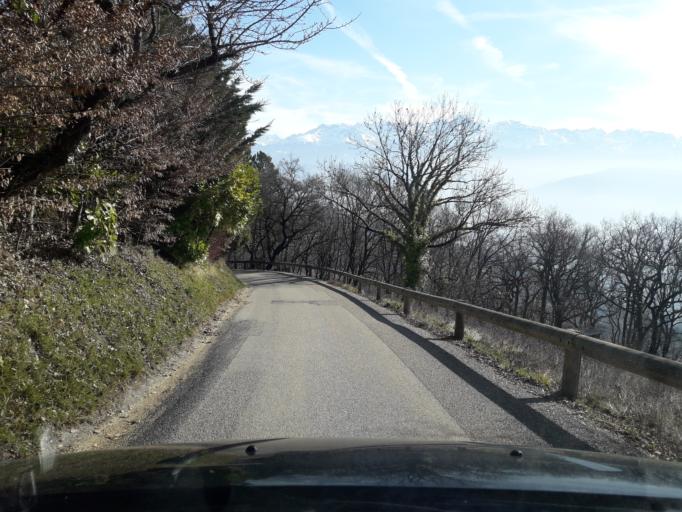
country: FR
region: Rhone-Alpes
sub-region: Departement de l'Isere
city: La Tronche
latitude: 45.2204
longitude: 5.7488
